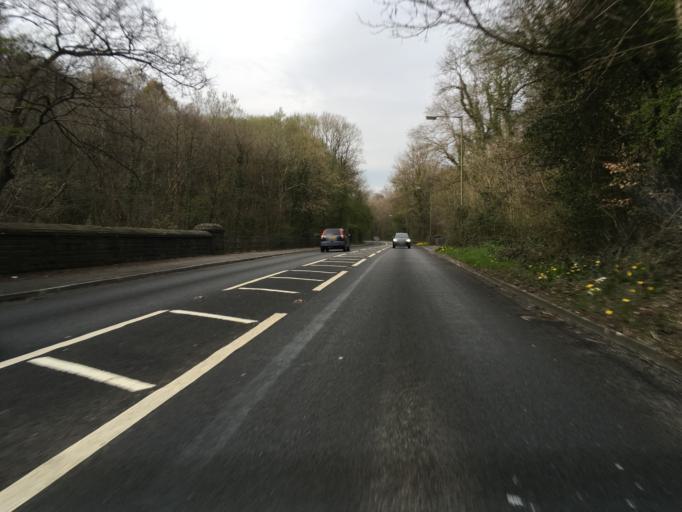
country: GB
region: Wales
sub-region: Caerphilly County Borough
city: Blackwood
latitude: 51.6394
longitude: -3.1879
